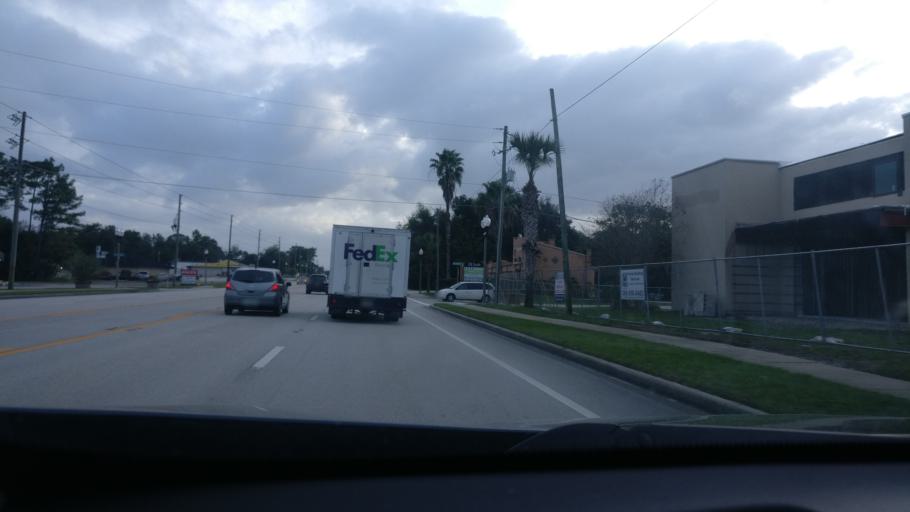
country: US
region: Florida
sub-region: Volusia County
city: DeBary
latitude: 28.8792
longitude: -81.3105
